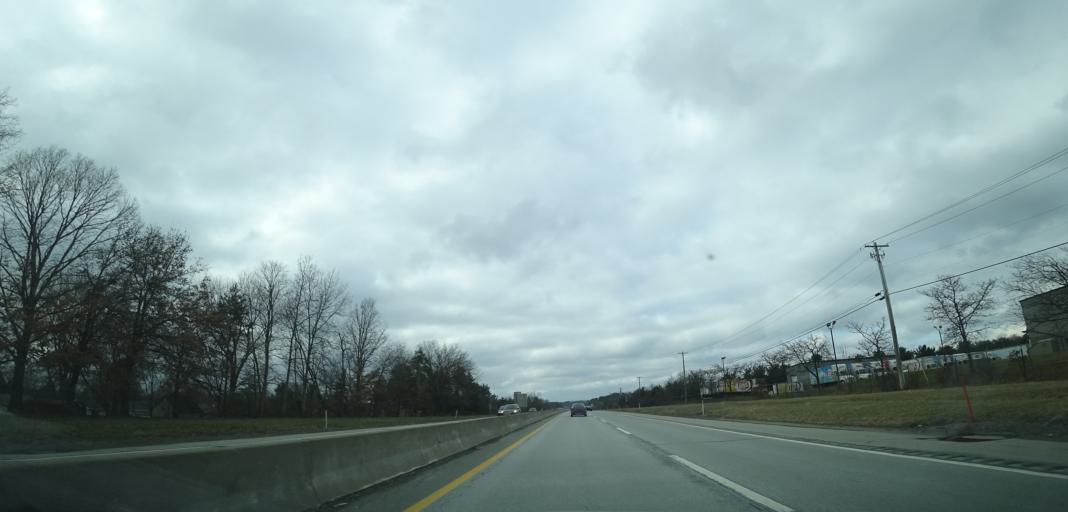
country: US
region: Pennsylvania
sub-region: Butler County
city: Cranberry Township
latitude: 40.6930
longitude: -80.1138
